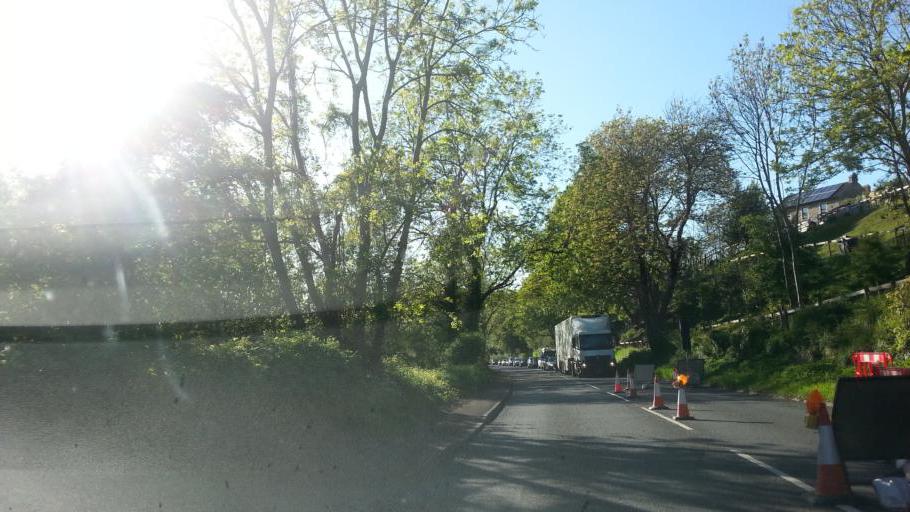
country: GB
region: England
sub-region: Bath and North East Somerset
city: Publow
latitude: 51.3638
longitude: -2.5441
